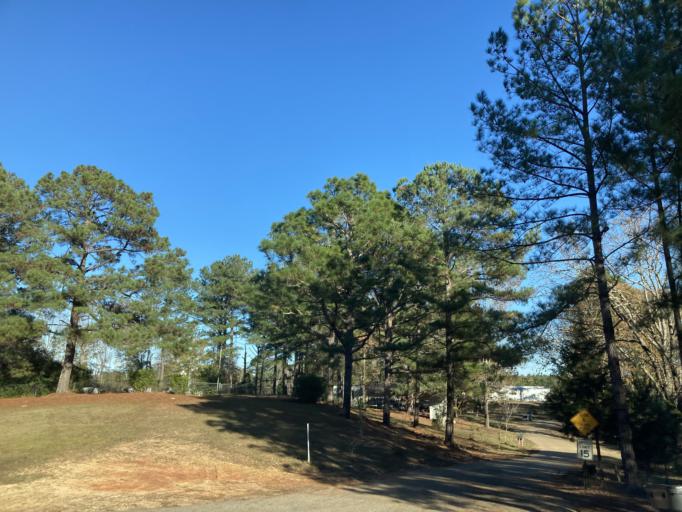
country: US
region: Mississippi
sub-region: Lamar County
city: Sumrall
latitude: 31.3896
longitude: -89.5673
